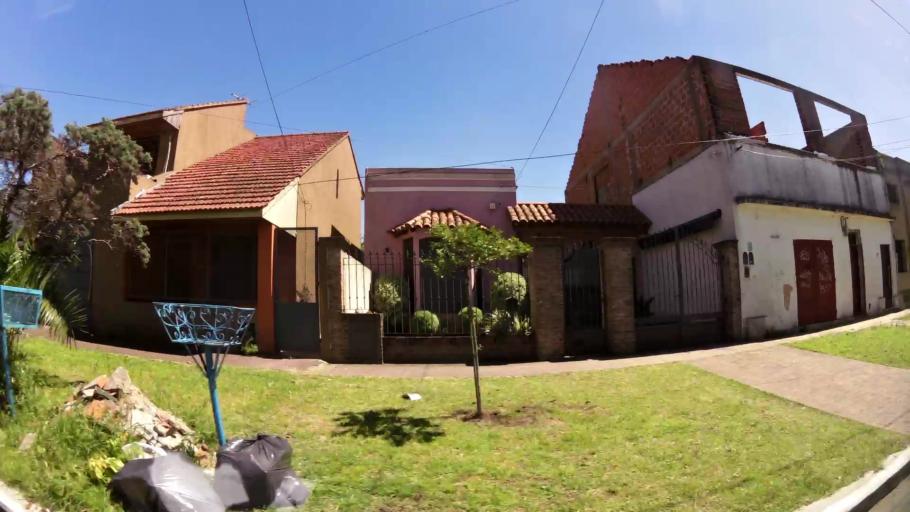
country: AR
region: Buenos Aires
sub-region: Partido de Quilmes
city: Quilmes
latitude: -34.7210
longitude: -58.2746
